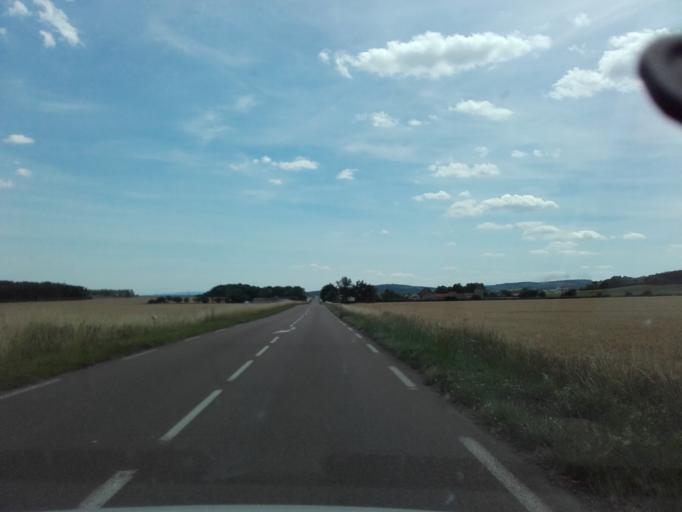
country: FR
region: Bourgogne
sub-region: Departement de Saone-et-Loire
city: Chagny
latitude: 46.8955
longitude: 4.7522
